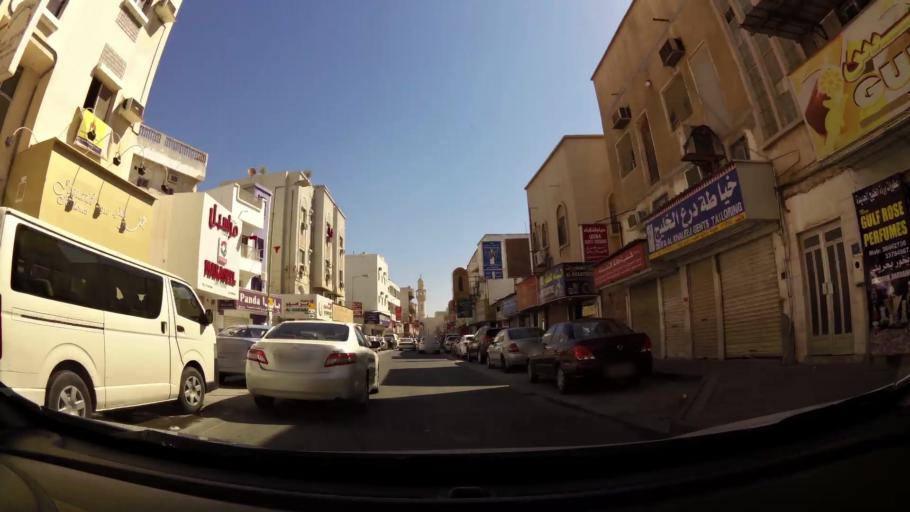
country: BH
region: Muharraq
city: Al Muharraq
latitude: 26.2512
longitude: 50.6107
